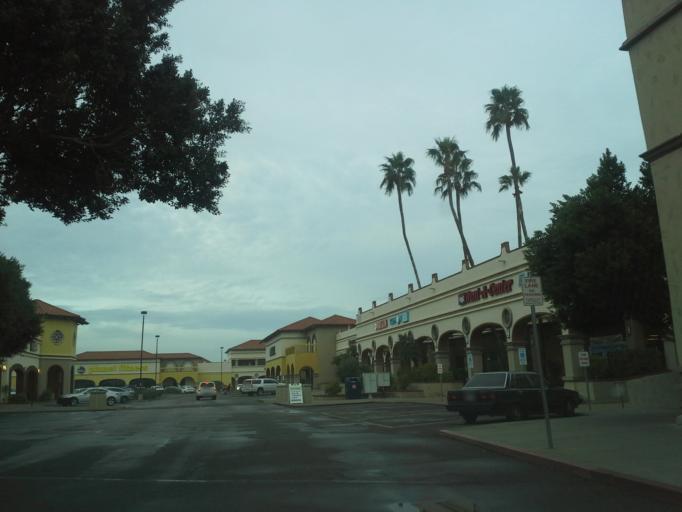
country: US
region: Arizona
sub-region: Maricopa County
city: Glendale
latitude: 33.6415
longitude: -112.0674
